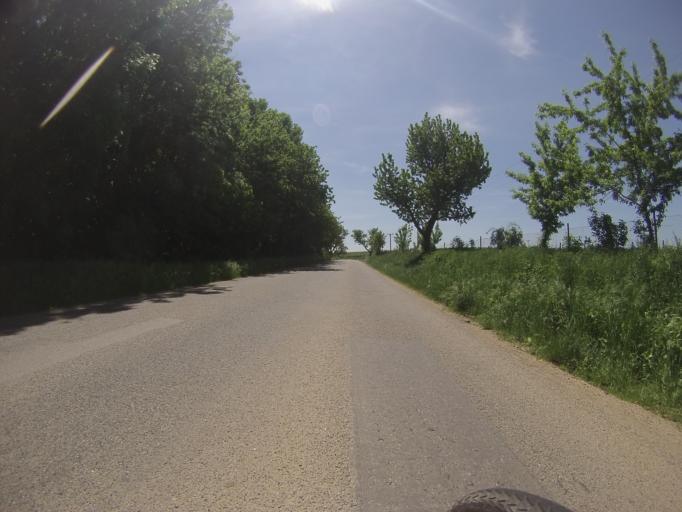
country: CZ
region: South Moravian
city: Vranovice
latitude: 48.9432
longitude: 16.5854
